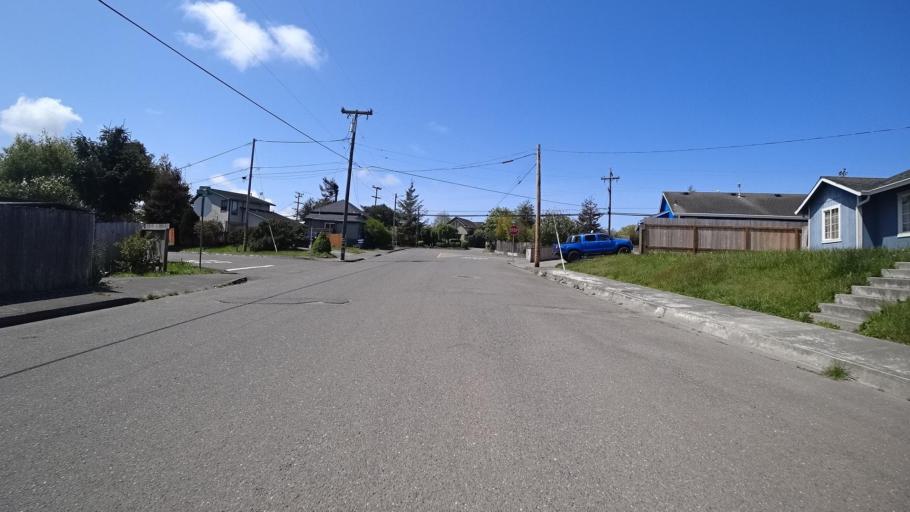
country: US
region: California
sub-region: Humboldt County
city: Bayview
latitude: 40.7764
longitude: -124.1743
